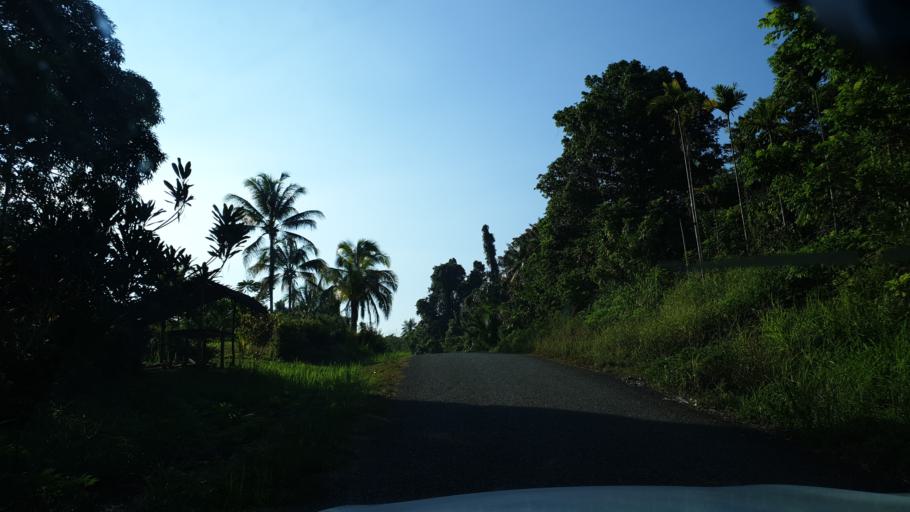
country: PG
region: East Sepik
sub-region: Wewak
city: Wewak
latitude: -3.6929
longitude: 143.6579
